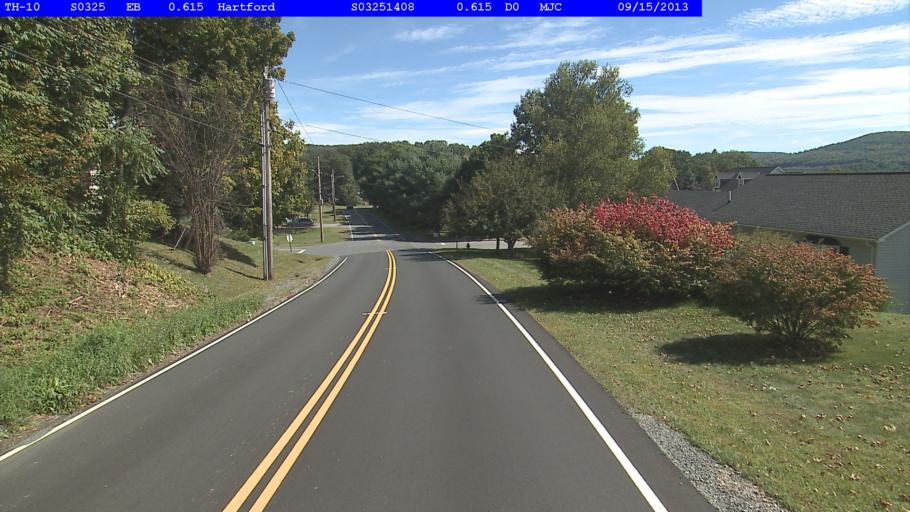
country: US
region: Vermont
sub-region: Windsor County
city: White River Junction
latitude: 43.6436
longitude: -72.3243
